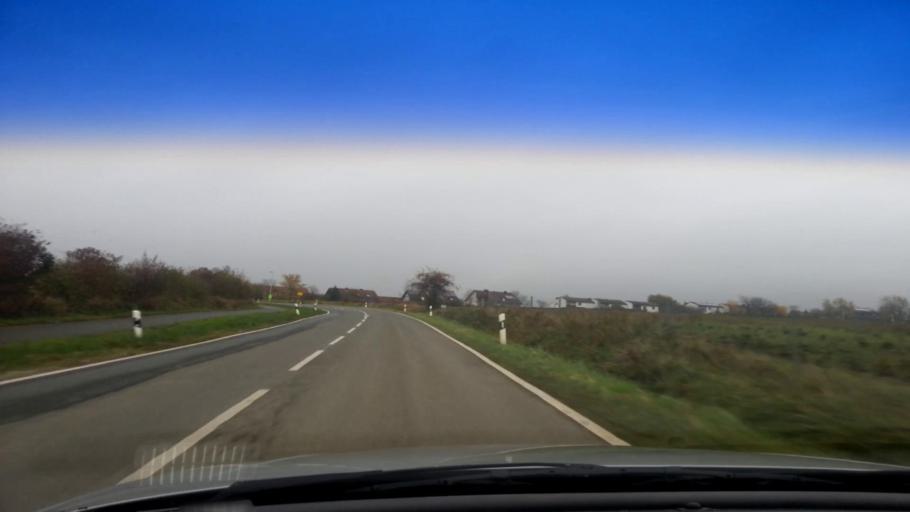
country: DE
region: Bavaria
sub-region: Upper Franconia
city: Litzendorf
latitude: 49.9059
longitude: 11.0124
